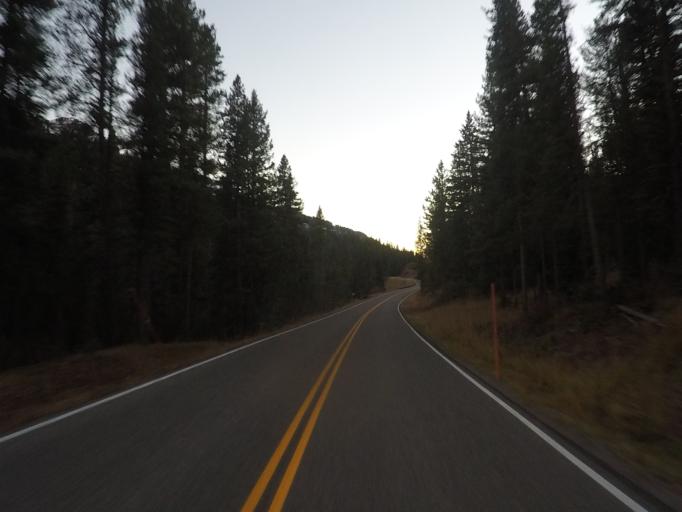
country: US
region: Montana
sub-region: Stillwater County
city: Absarokee
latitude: 44.9314
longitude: -110.0852
